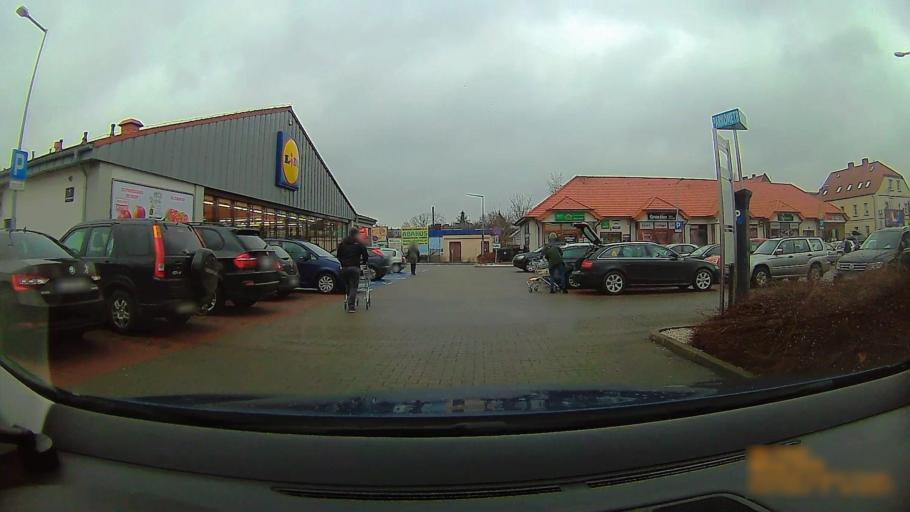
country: PL
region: Greater Poland Voivodeship
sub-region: Konin
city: Konin
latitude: 52.2075
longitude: 18.2536
